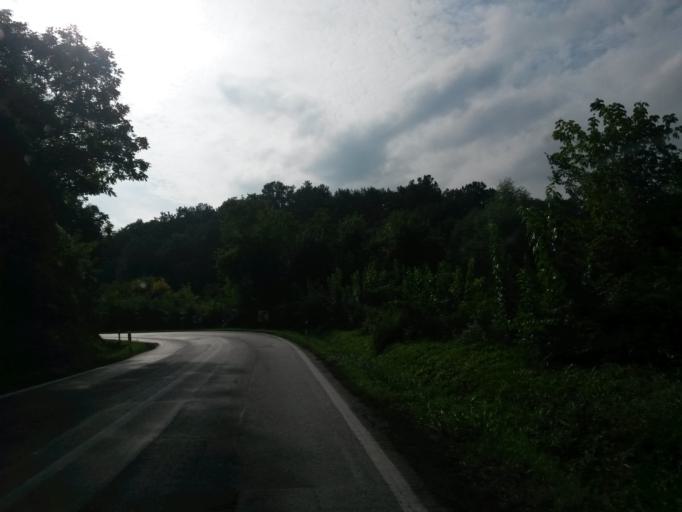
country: HR
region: Vukovarsko-Srijemska
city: Ilok
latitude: 45.2252
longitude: 19.3402
